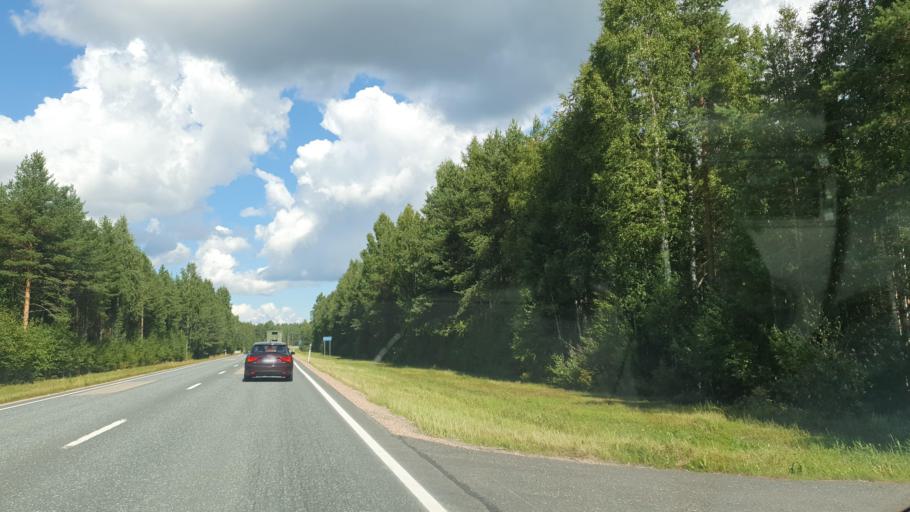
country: FI
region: Kainuu
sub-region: Kajaani
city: Kajaani
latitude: 64.1116
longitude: 27.4483
